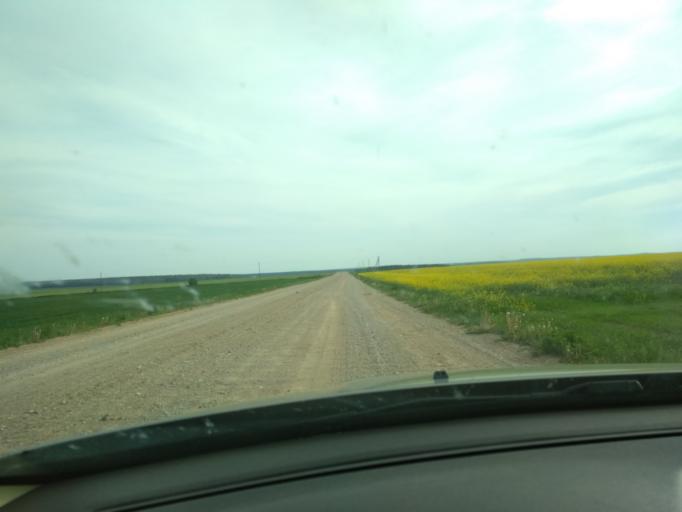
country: BY
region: Grodnenskaya
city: Mir
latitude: 53.4081
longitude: 26.4194
